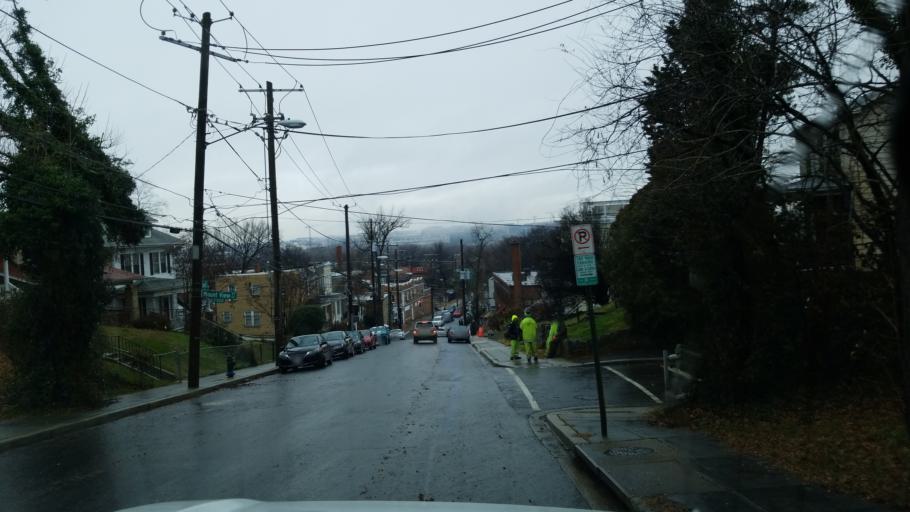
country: US
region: Maryland
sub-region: Prince George's County
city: Hillcrest Heights
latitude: 38.8620
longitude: -76.9912
